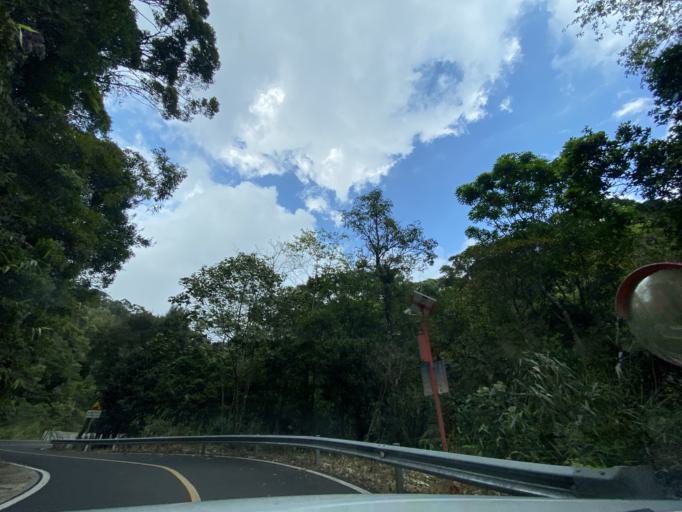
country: CN
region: Hainan
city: Diaoluoshan
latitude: 18.7217
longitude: 109.8728
